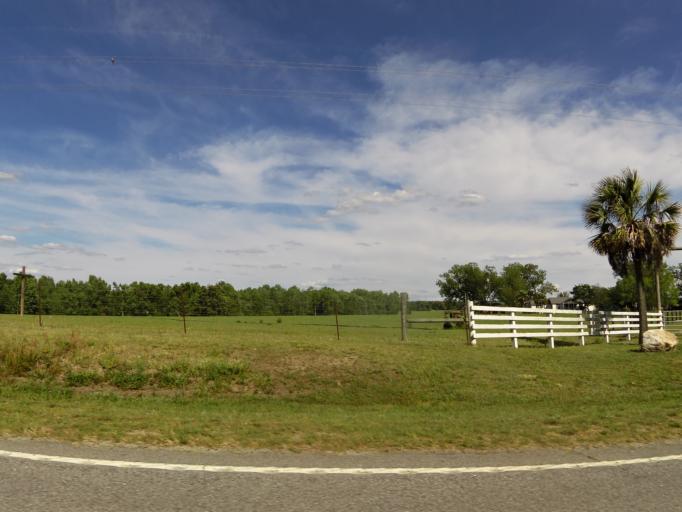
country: US
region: South Carolina
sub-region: Bamberg County
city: Denmark
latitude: 33.2636
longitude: -81.1566
